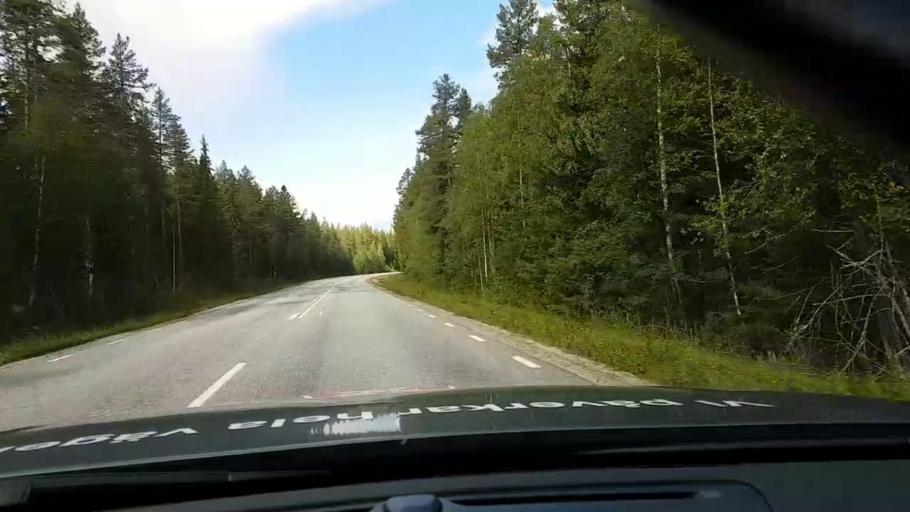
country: SE
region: Vaesternorrland
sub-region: OErnskoeldsviks Kommun
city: Bredbyn
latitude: 63.6036
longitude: 17.9039
